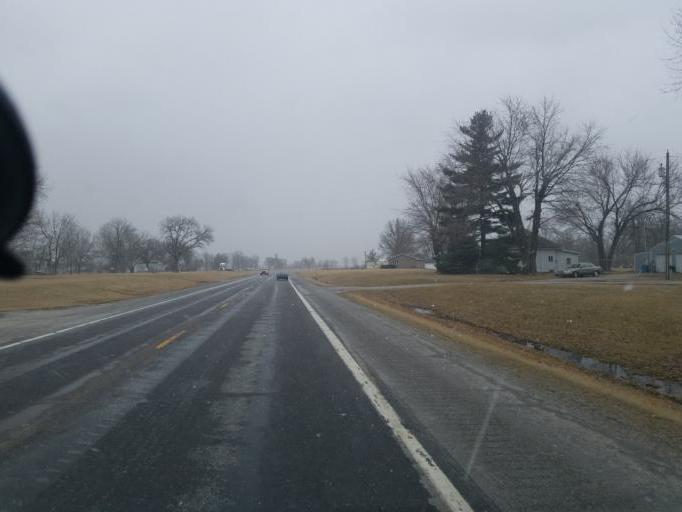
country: US
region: Missouri
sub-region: Schuyler County
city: Lancaster
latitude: 40.4124
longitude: -92.5630
